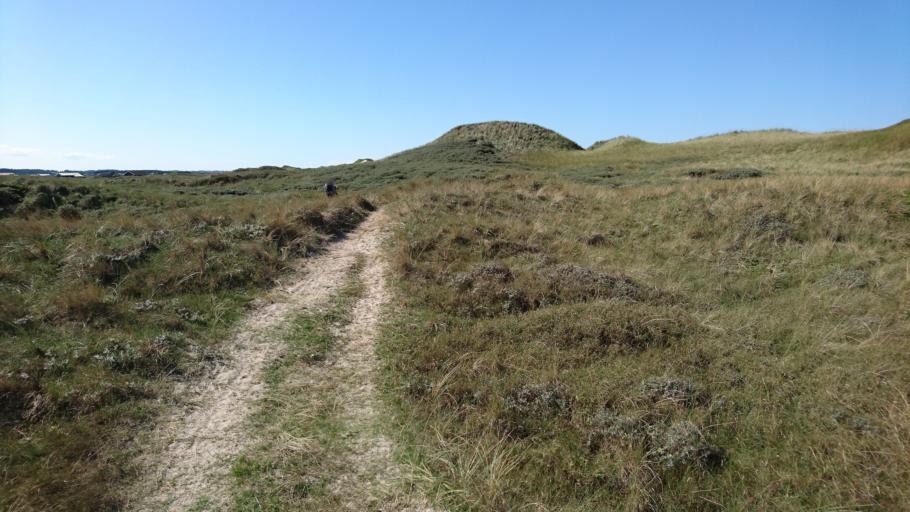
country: DK
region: North Denmark
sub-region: Hjorring Kommune
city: Hirtshals
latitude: 57.5178
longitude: 9.8706
